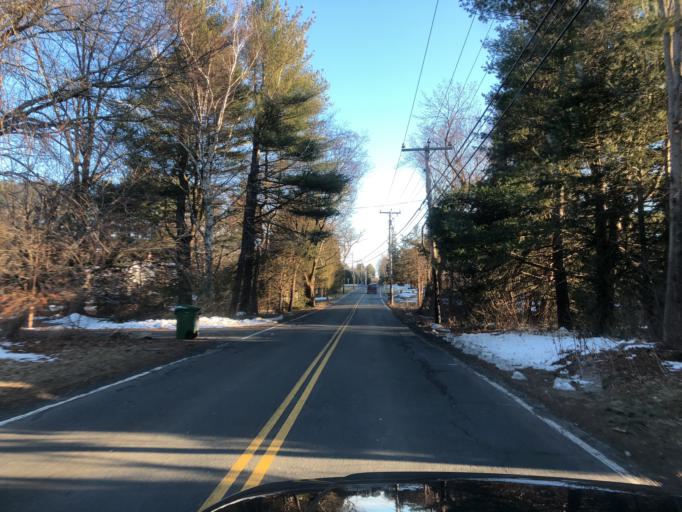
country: US
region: Connecticut
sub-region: Hartford County
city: Farmington
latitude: 41.7679
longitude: -72.8593
